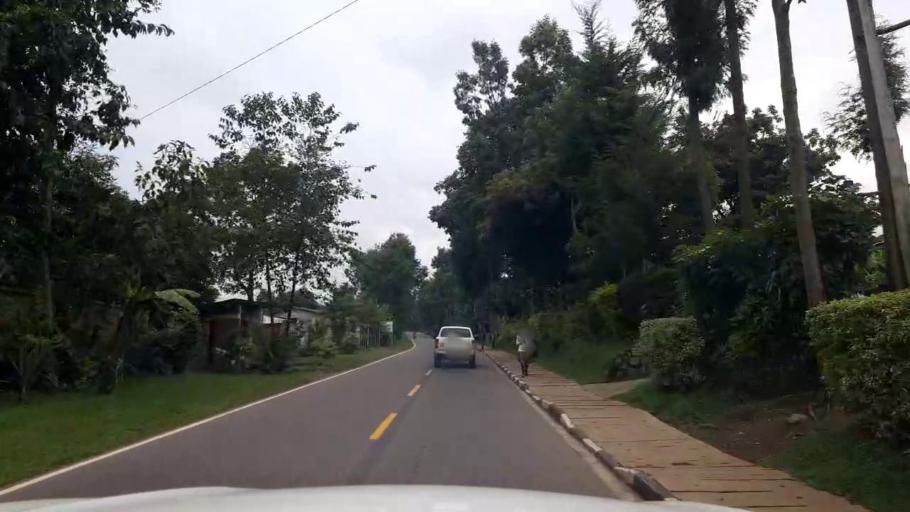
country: RW
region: Northern Province
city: Musanze
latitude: -1.4586
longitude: 29.6118
